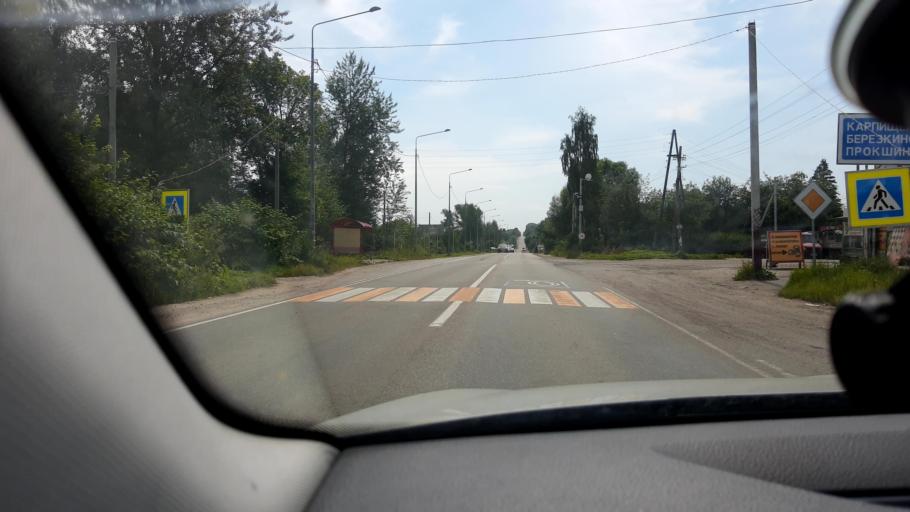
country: RU
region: Tula
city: Zaokskiy
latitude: 54.8047
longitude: 37.4313
